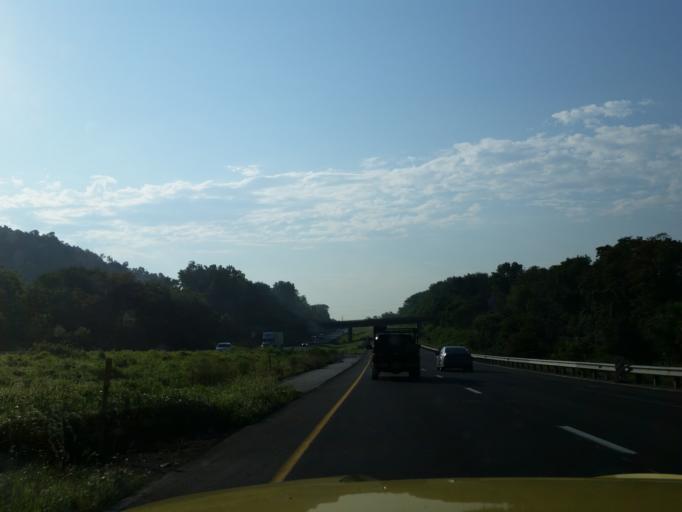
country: US
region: Pennsylvania
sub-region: Lancaster County
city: Columbia
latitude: 40.0431
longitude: -76.4849
